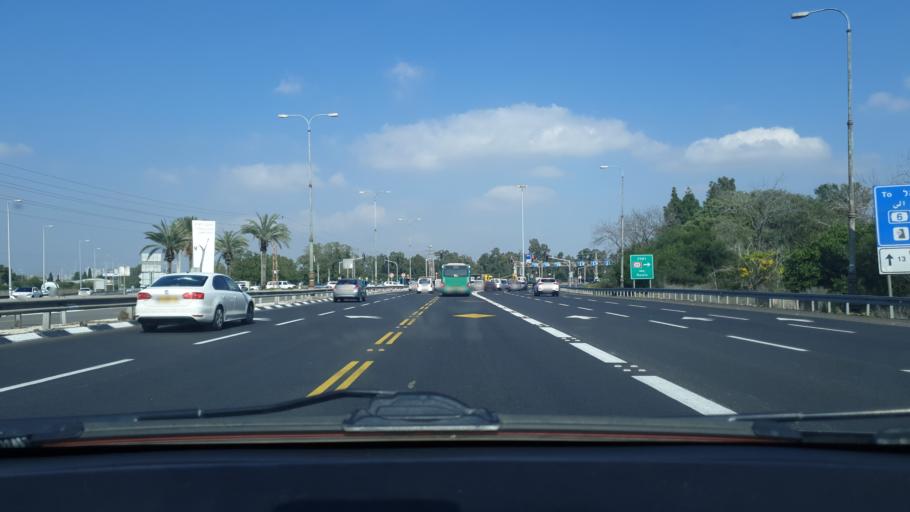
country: IL
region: Central District
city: Bet Dagan
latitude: 31.9994
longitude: 34.8197
